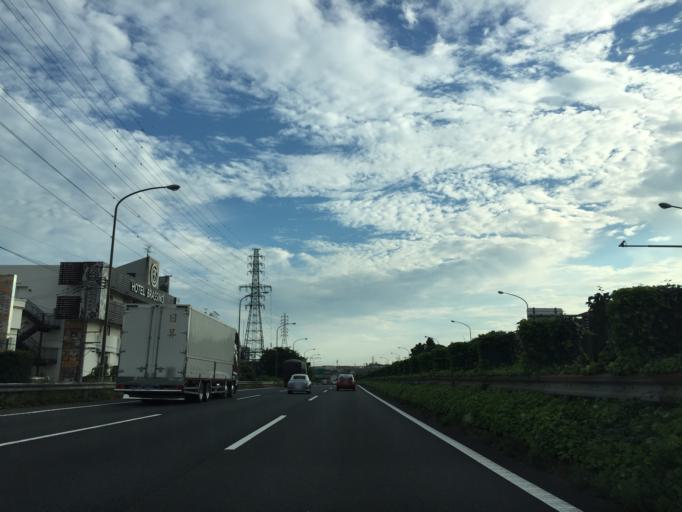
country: JP
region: Kanagawa
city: Minami-rinkan
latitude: 35.5038
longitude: 139.4803
